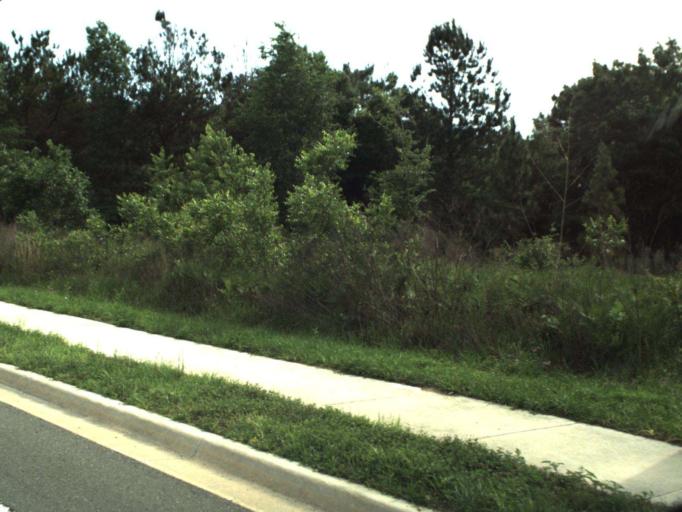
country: US
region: Florida
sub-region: Marion County
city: Silver Springs Shores
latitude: 29.1636
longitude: -82.0537
